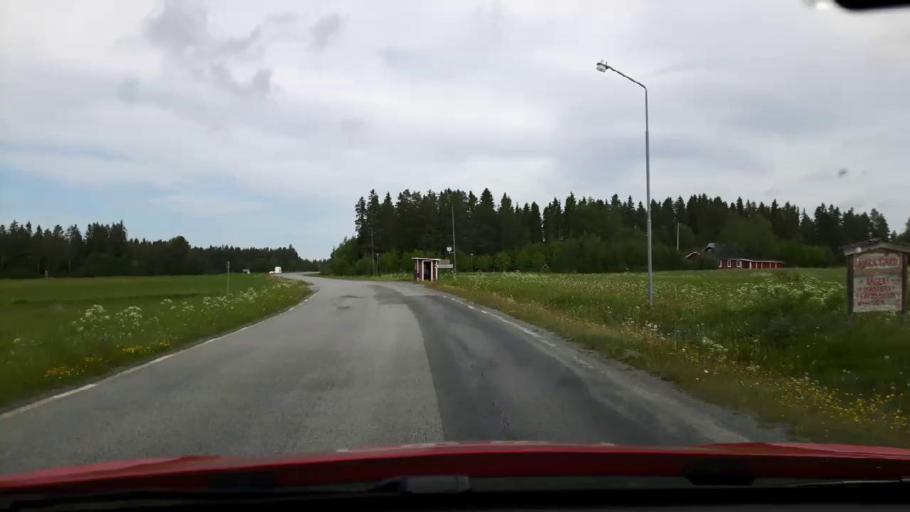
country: SE
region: Jaemtland
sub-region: OEstersunds Kommun
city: Ostersund
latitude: 63.0577
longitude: 14.4505
